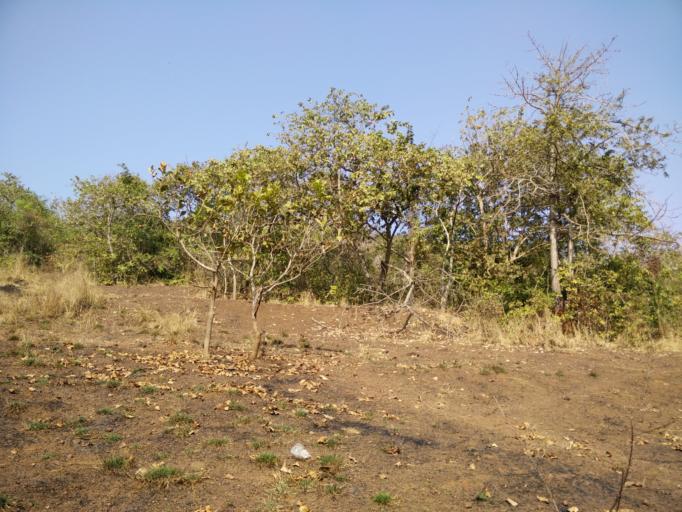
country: IN
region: Goa
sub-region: North Goa
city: Candolim
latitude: 15.4946
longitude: 73.7703
